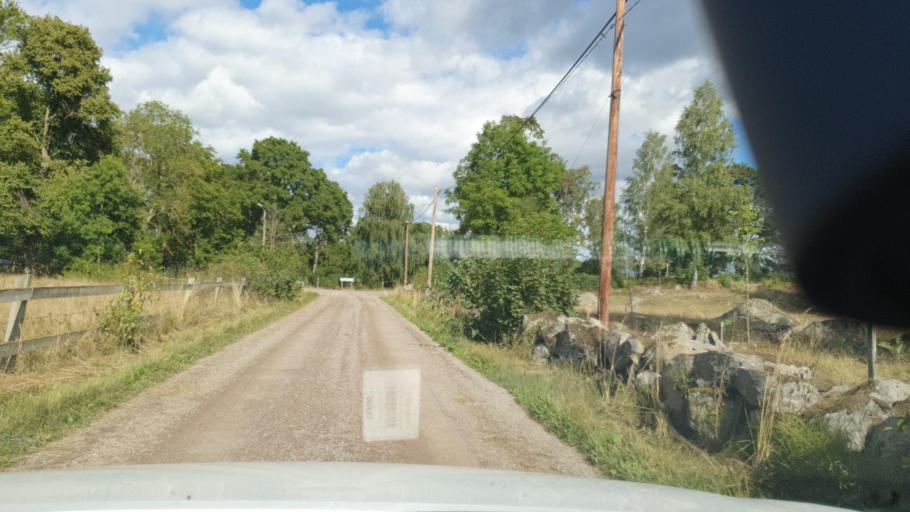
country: SE
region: Kalmar
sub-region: Hultsfreds Kommun
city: Malilla
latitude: 57.3237
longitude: 15.8095
